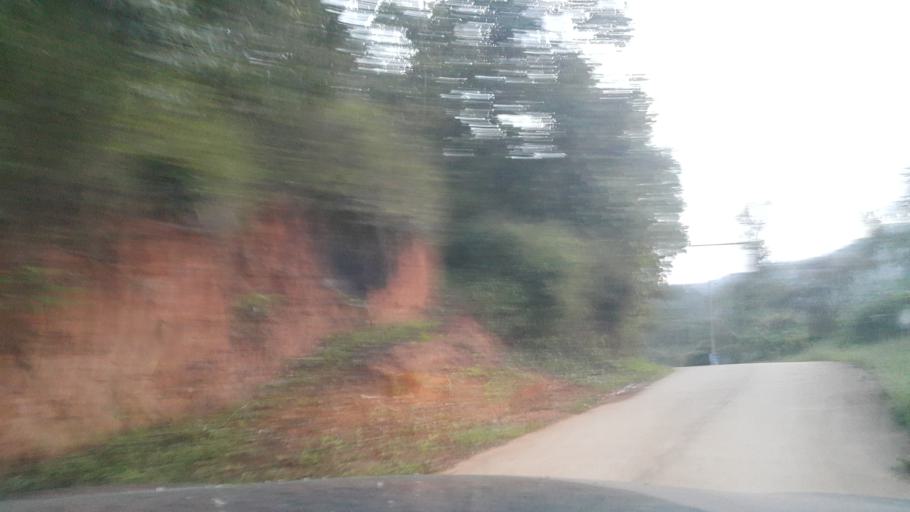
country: TH
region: Chiang Mai
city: Samoeng
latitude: 18.9489
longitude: 98.6747
